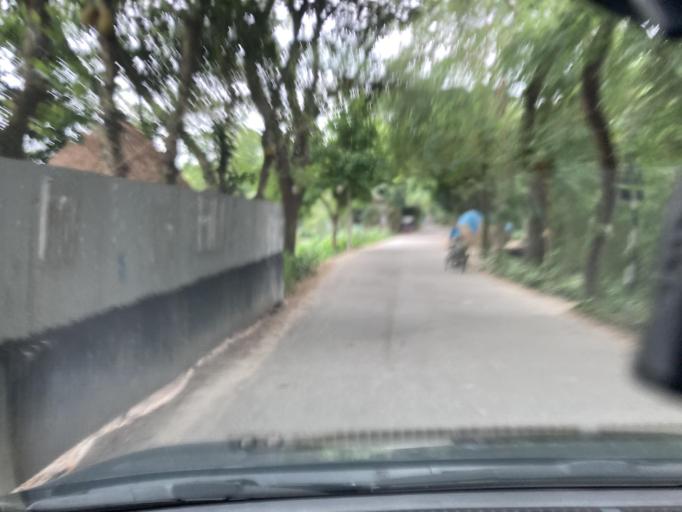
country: BD
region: Dhaka
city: Dohar
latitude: 23.7990
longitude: 90.0478
